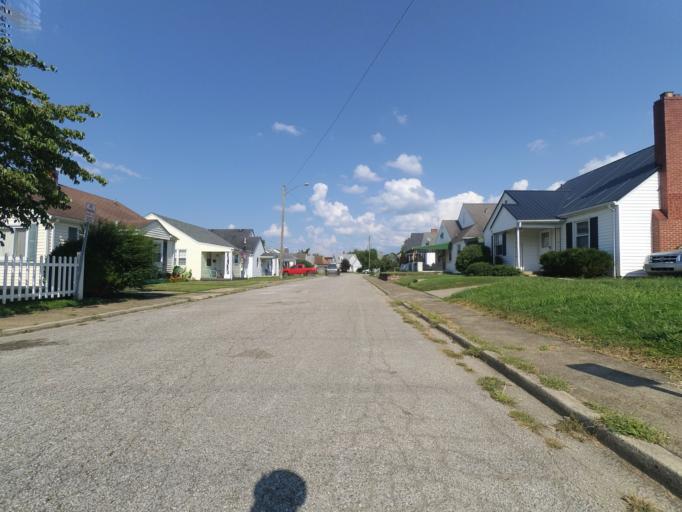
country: US
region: West Virginia
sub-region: Cabell County
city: Huntington
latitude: 38.4157
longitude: -82.4605
